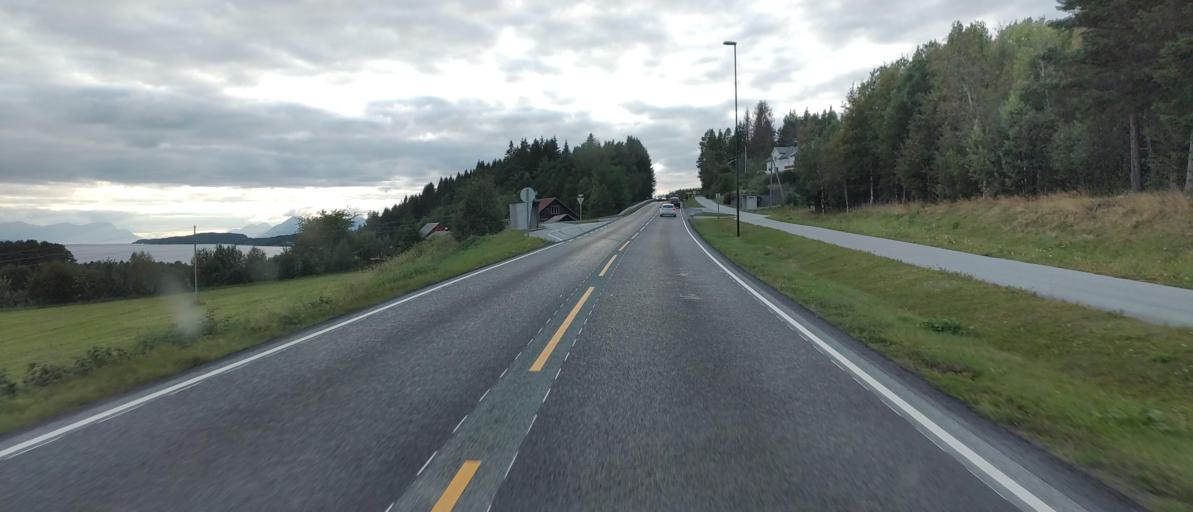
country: NO
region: More og Romsdal
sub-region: Molde
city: Hjelset
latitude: 62.7331
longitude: 7.4040
